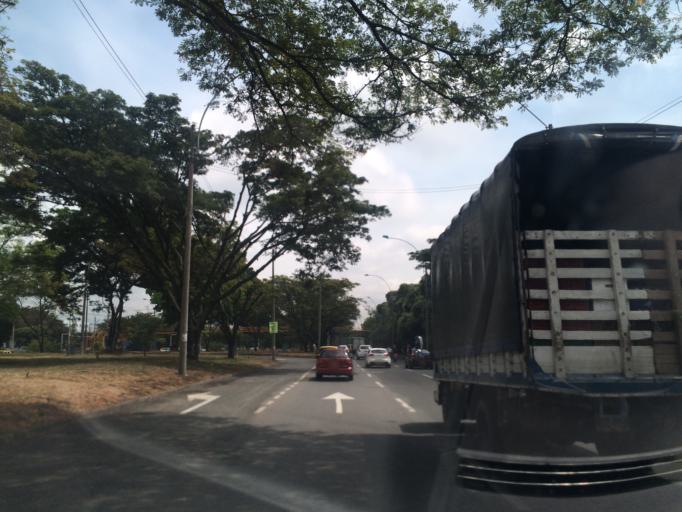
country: CO
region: Valle del Cauca
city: Cali
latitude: 3.3776
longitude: -76.5248
